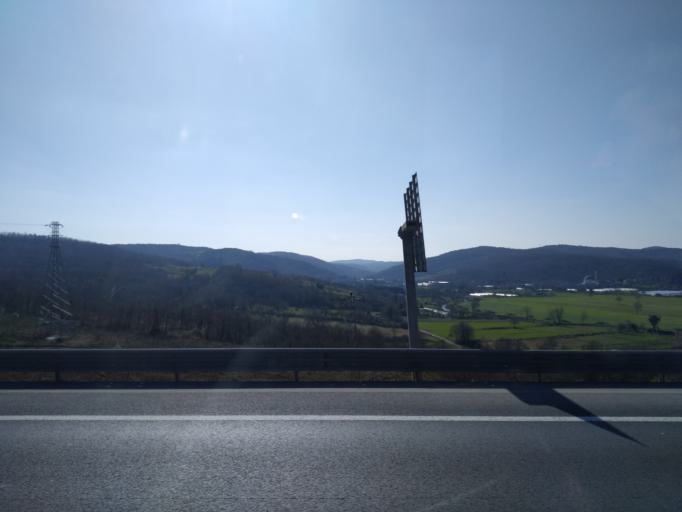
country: TR
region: Istanbul
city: Mahmut Sevket Pasa
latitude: 41.1868
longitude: 29.2150
